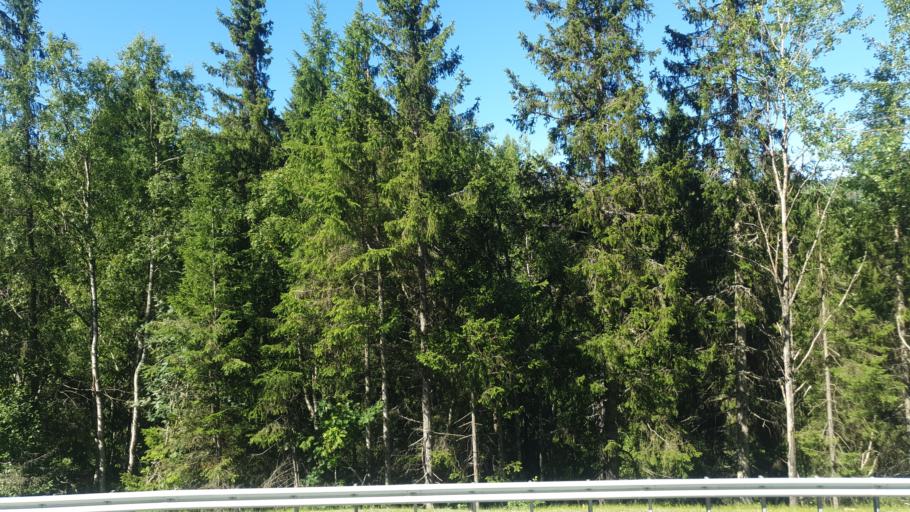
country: NO
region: Sor-Trondelag
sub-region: Meldal
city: Meldal
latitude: 63.1530
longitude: 9.7206
